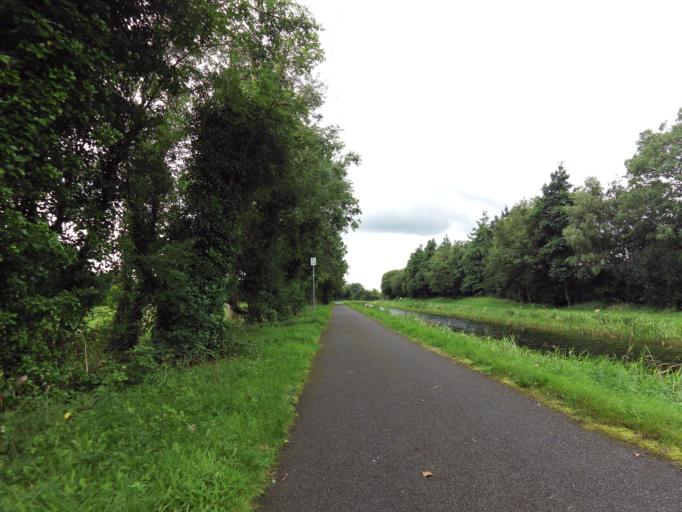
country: IE
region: Leinster
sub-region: An Iarmhi
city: An Muileann gCearr
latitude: 53.5116
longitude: -7.3795
